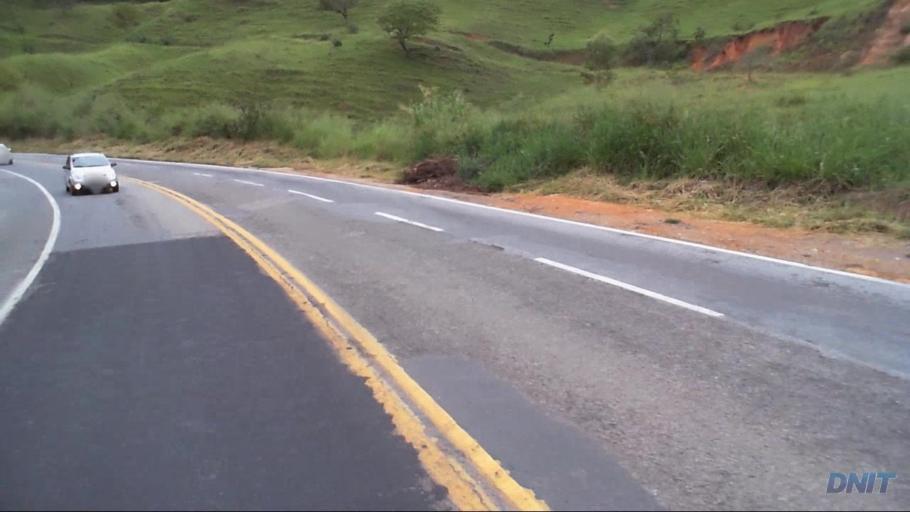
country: BR
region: Minas Gerais
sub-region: Joao Monlevade
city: Joao Monlevade
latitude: -19.8572
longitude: -43.2176
